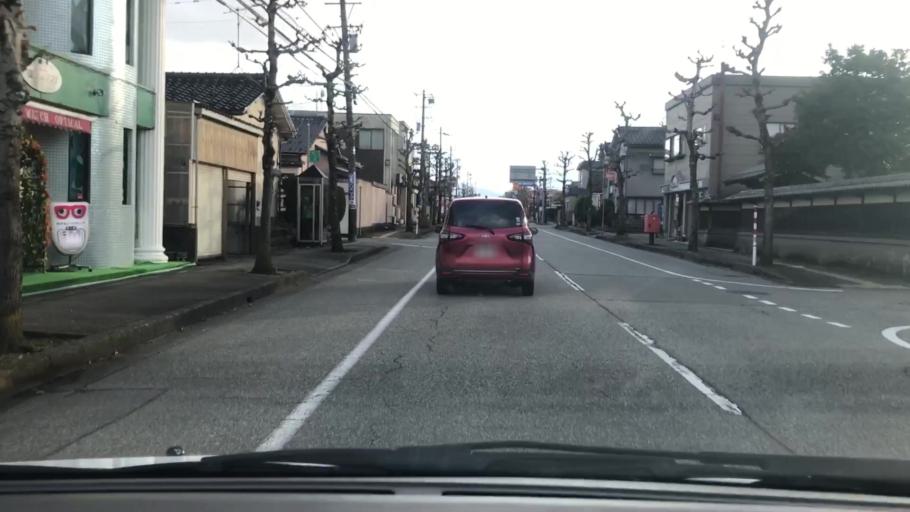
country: JP
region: Toyama
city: Toyama-shi
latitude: 36.6757
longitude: 137.2370
